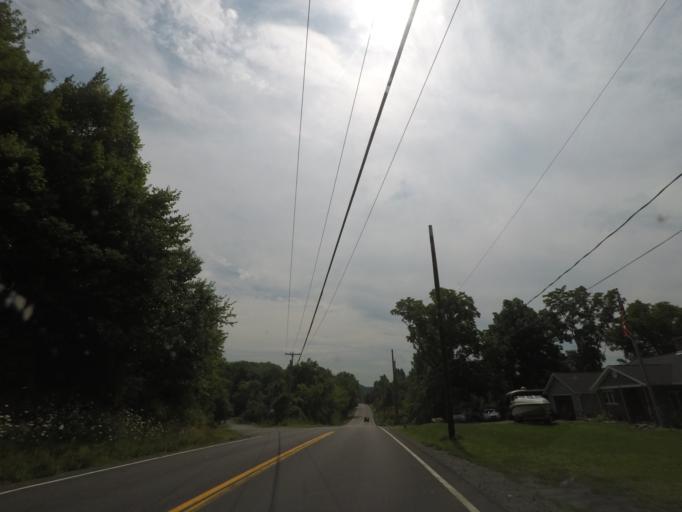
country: US
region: New York
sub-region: Saratoga County
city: Waterford
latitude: 42.7688
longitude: -73.6359
